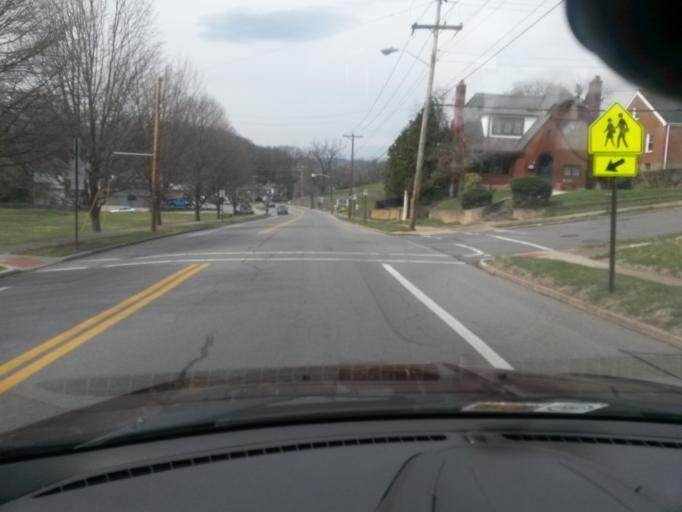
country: US
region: Virginia
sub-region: Roanoke County
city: Cave Spring
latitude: 37.2553
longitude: -79.9880
